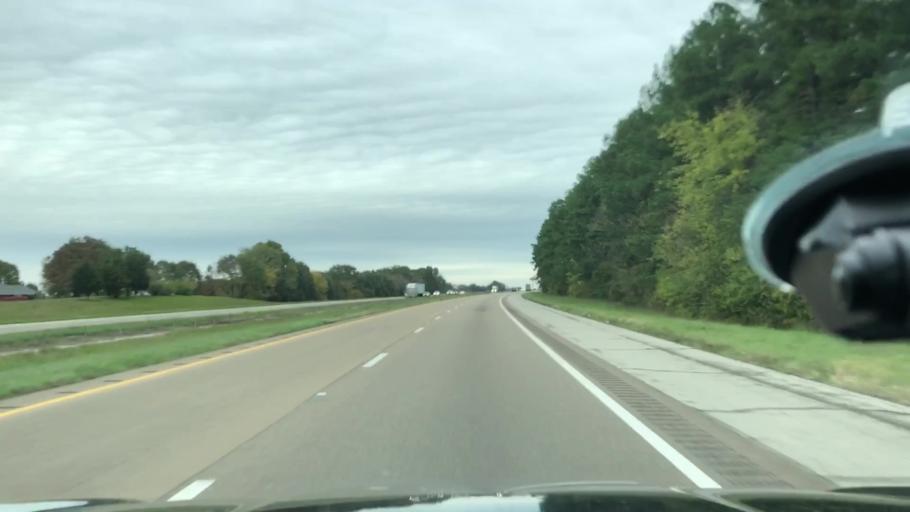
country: US
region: Texas
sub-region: Titus County
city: Mount Pleasant
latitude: 33.2309
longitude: -94.8828
